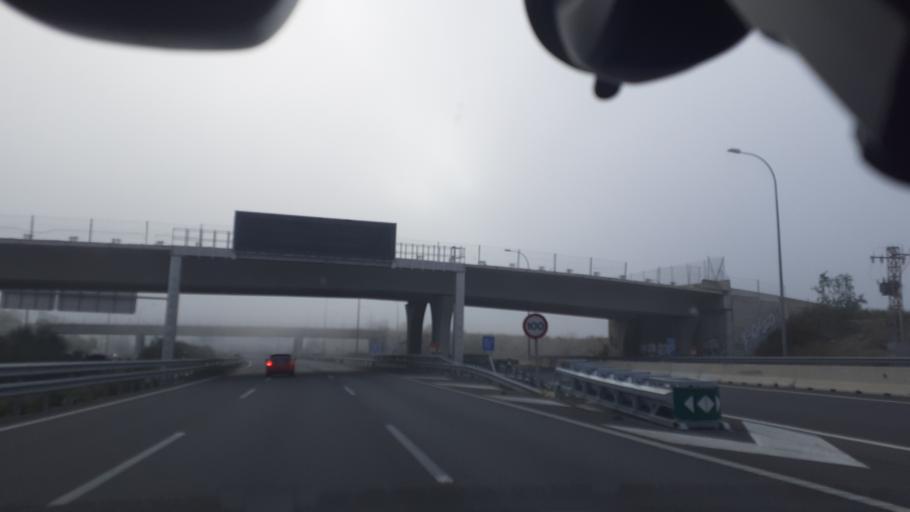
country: ES
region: Madrid
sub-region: Provincia de Madrid
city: Vicalvaro
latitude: 40.3890
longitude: -3.5840
